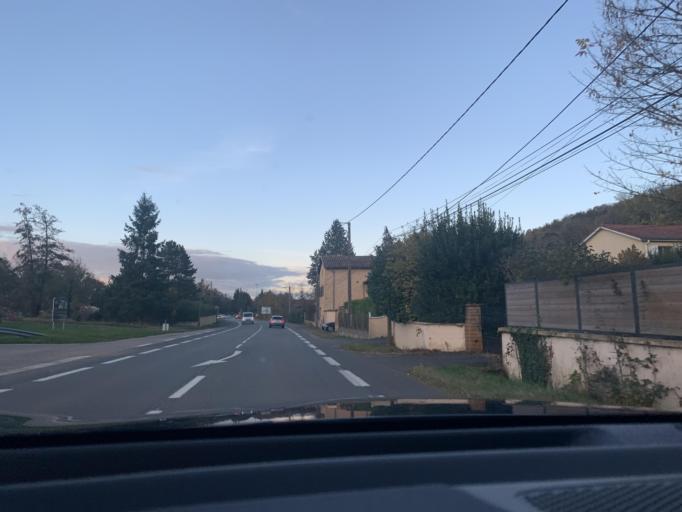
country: FR
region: Rhone-Alpes
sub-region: Departement du Rhone
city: Liergues
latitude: 45.9670
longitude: 4.6713
